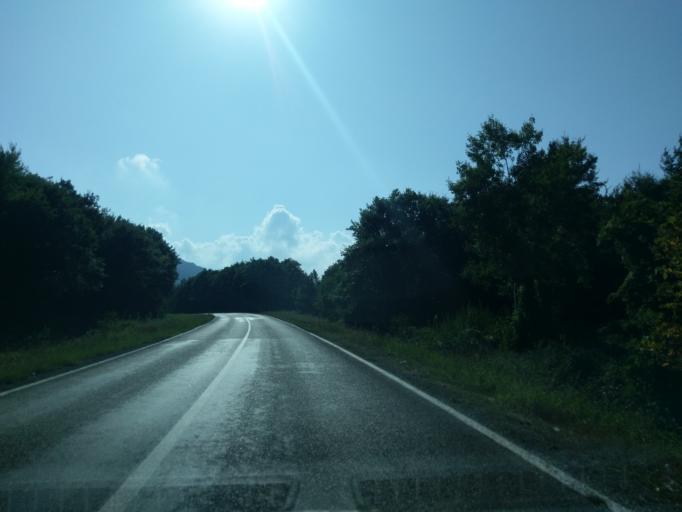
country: TR
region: Sinop
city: Yenikonak
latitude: 41.9446
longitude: 34.7362
